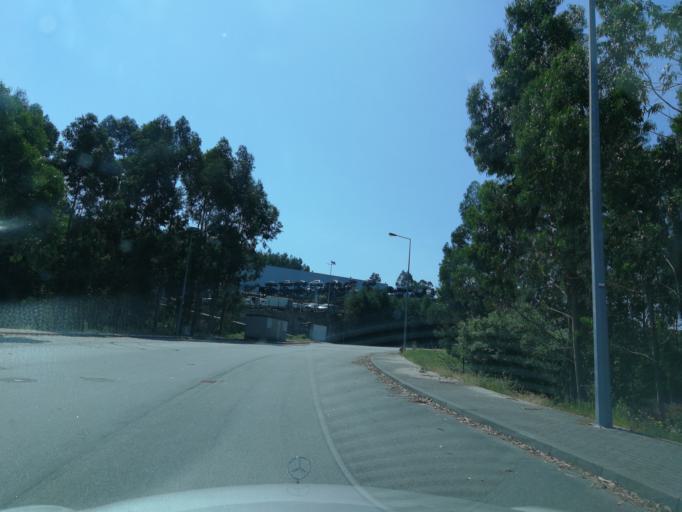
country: PT
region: Braga
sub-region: Braga
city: Adaufe
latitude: 41.5607
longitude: -8.3456
